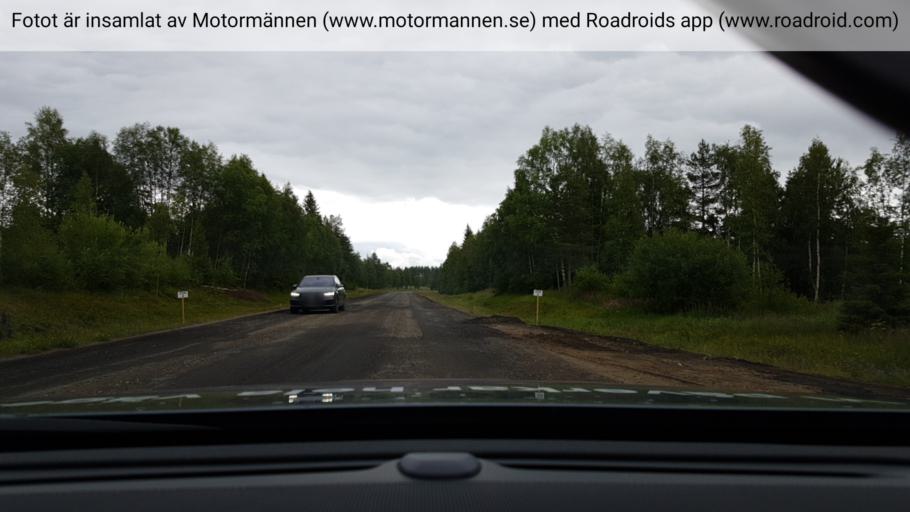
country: SE
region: Vaesterbotten
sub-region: Norsjo Kommun
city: Norsjoe
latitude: 65.2048
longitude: 19.8054
